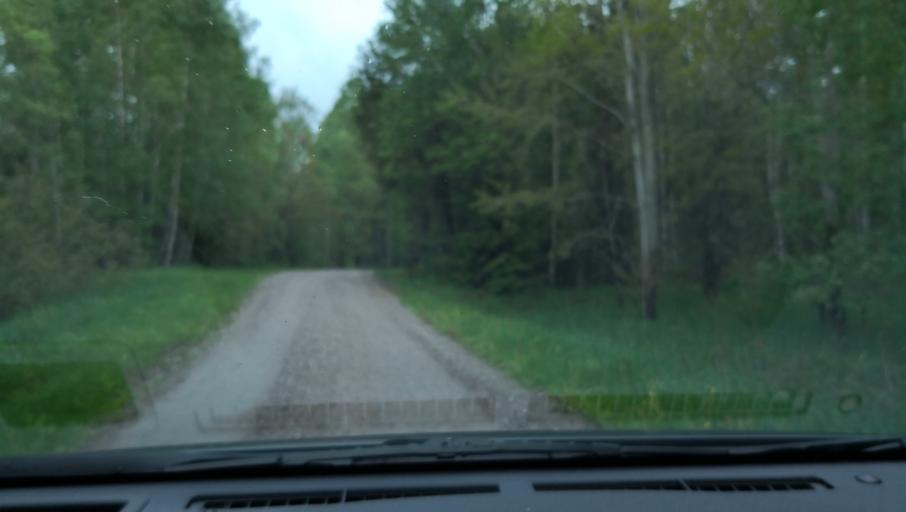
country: SE
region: Uppsala
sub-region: Heby Kommun
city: OEstervala
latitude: 59.9925
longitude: 17.2515
